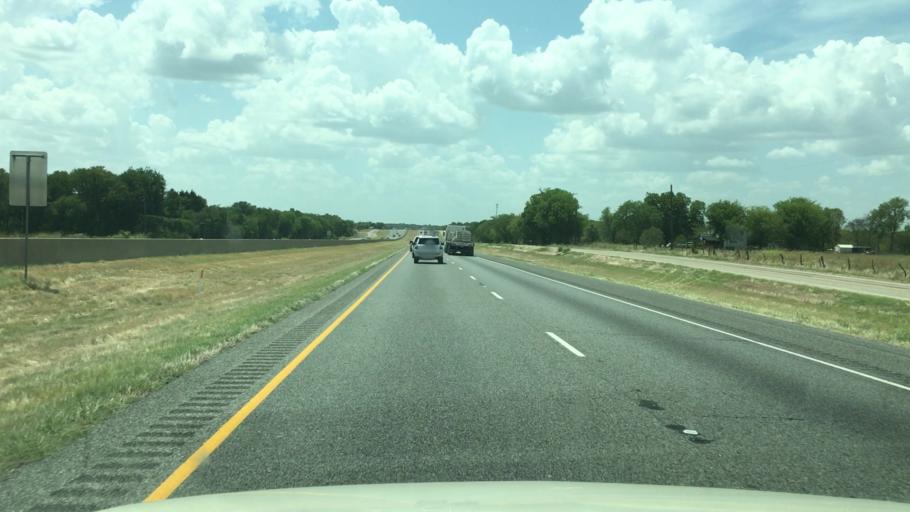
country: US
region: Texas
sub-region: Hunt County
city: Commerce
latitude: 33.1317
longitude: -95.9259
